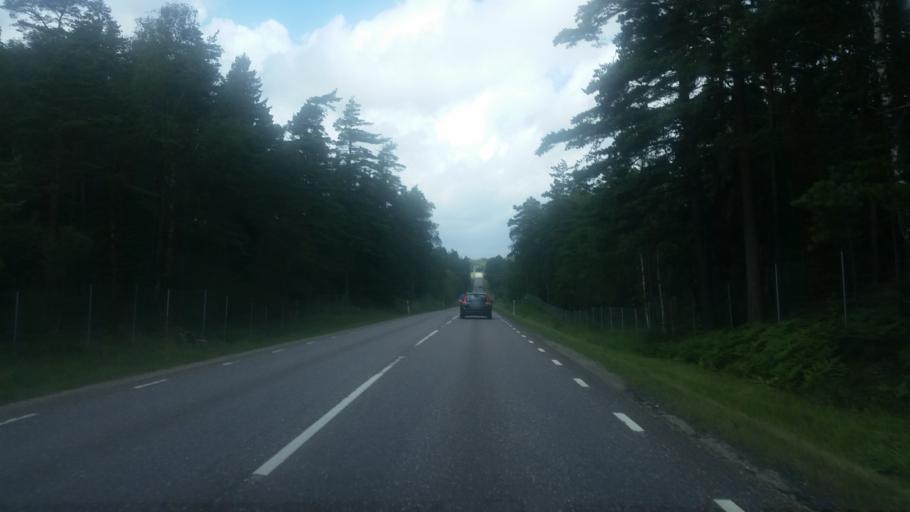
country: SE
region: Vaestra Goetaland
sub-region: Partille Kommun
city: Furulund
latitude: 57.6961
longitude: 12.1565
